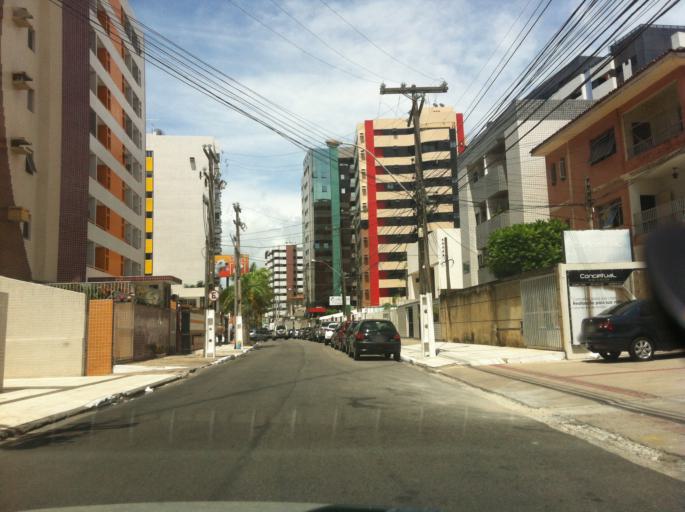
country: BR
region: Alagoas
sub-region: Maceio
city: Maceio
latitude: -9.6614
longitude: -35.7057
